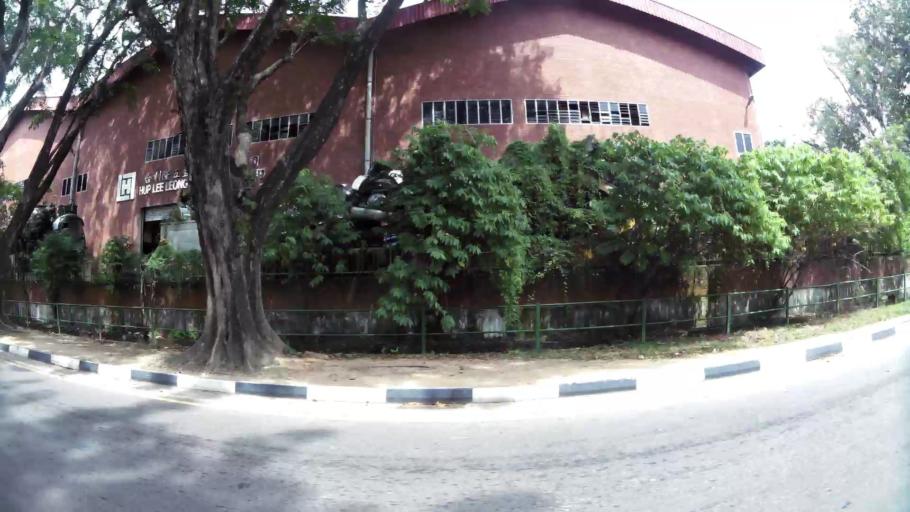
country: MY
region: Johor
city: Johor Bahru
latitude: 1.4162
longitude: 103.7441
